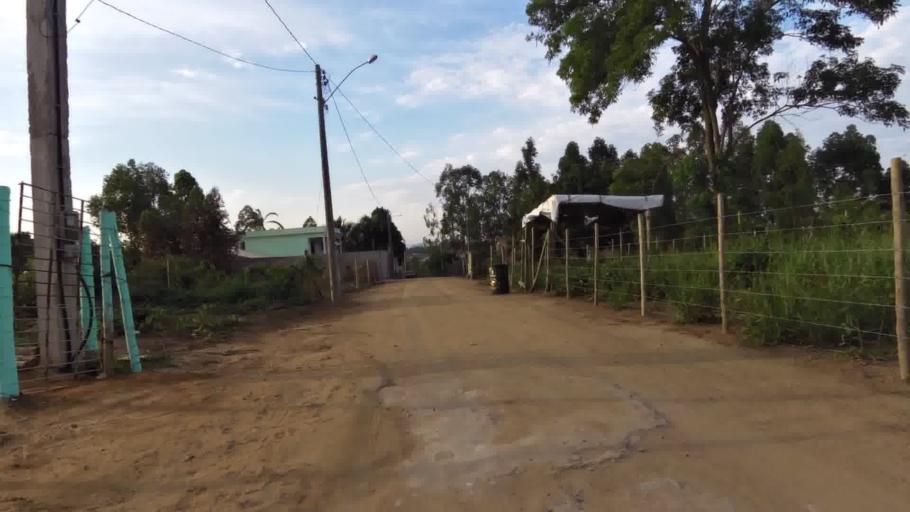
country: BR
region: Espirito Santo
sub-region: Piuma
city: Piuma
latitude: -20.8236
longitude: -40.7351
